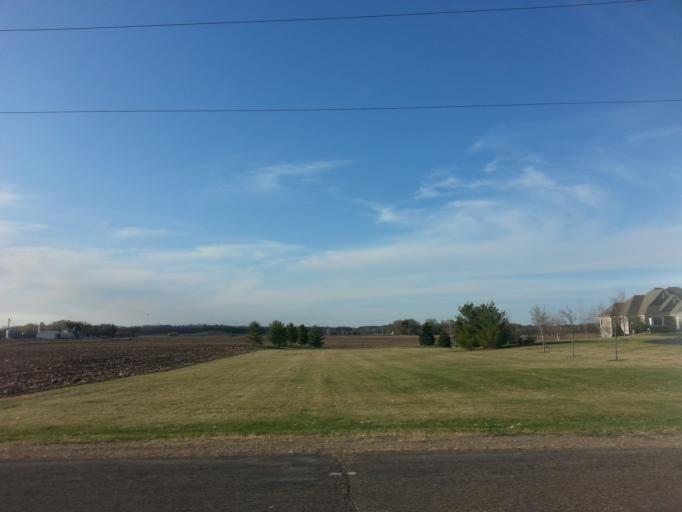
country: US
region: Minnesota
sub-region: Washington County
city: Lake Saint Croix Beach
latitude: 44.8624
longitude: -92.7141
